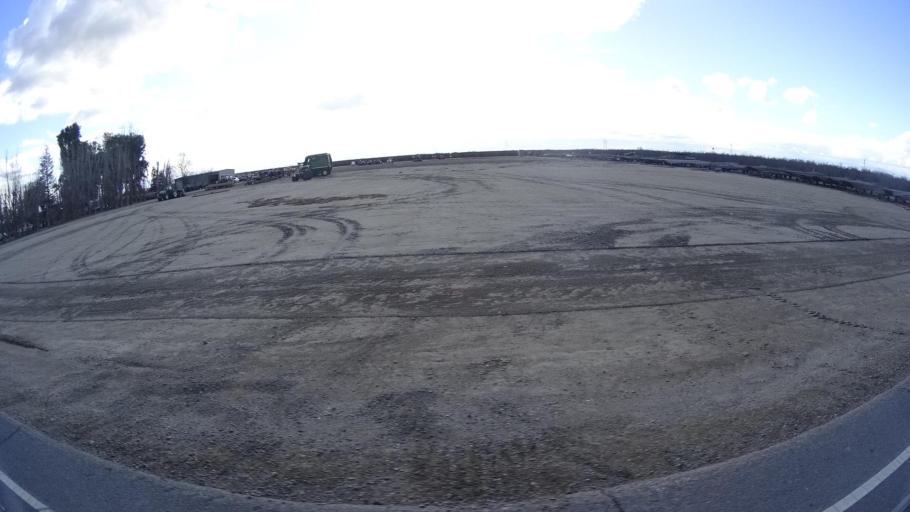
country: US
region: California
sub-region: Kern County
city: Greenacres
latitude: 35.2672
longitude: -119.1234
